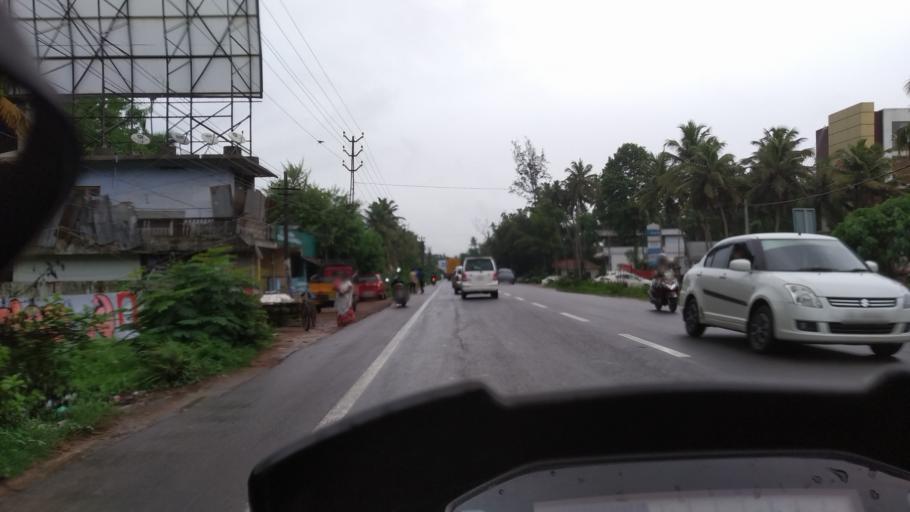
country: IN
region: Kerala
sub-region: Alappuzha
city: Kayankulam
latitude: 9.1226
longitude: 76.5177
